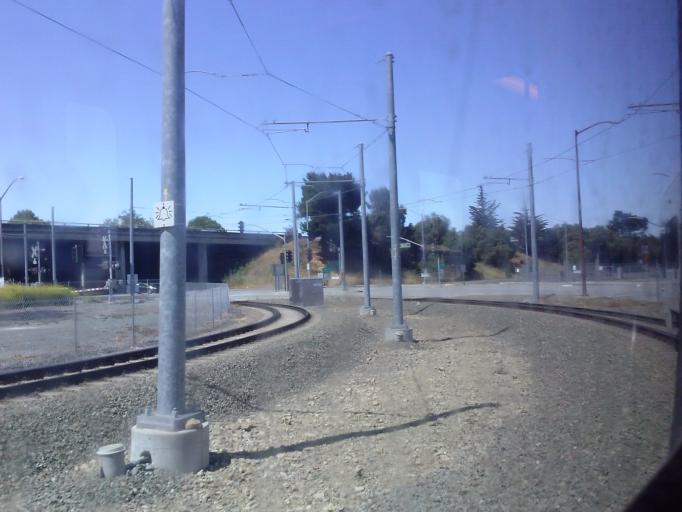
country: US
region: California
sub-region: Santa Clara County
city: Mountain View
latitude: 37.4049
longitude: -122.0507
